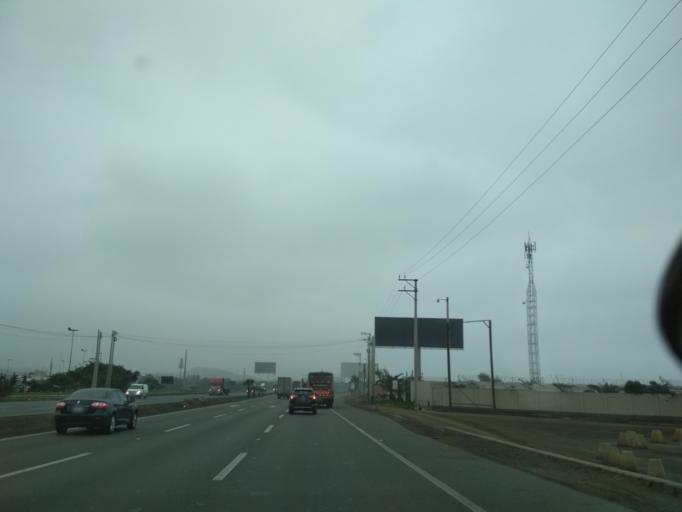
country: PE
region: Lima
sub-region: Lima
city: Punta Hermosa
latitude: -12.2536
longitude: -76.9265
